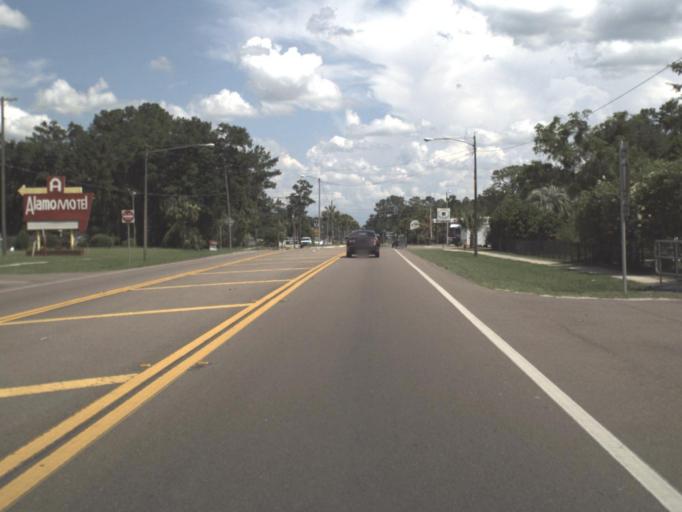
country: US
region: Florida
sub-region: Alachua County
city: High Springs
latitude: 29.8376
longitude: -82.6012
